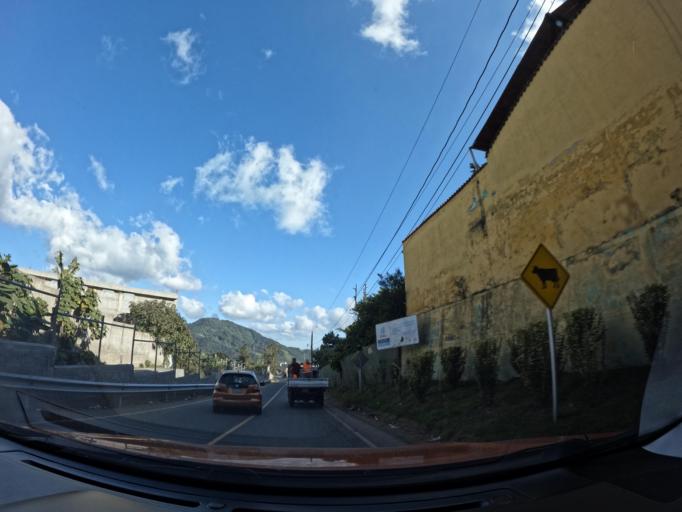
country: GT
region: Sacatepequez
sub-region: Municipio de Santa Maria de Jesus
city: Santa Maria de Jesus
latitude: 14.4887
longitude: -90.7090
